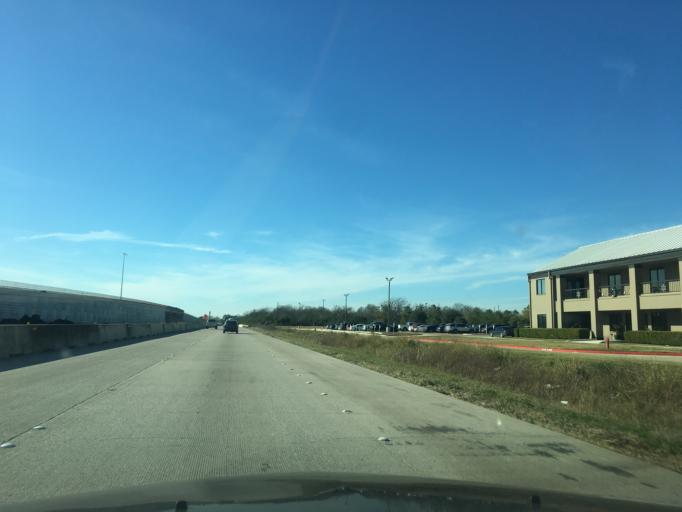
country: US
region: Texas
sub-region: Fort Bend County
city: Rosenberg
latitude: 29.5346
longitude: -95.8428
